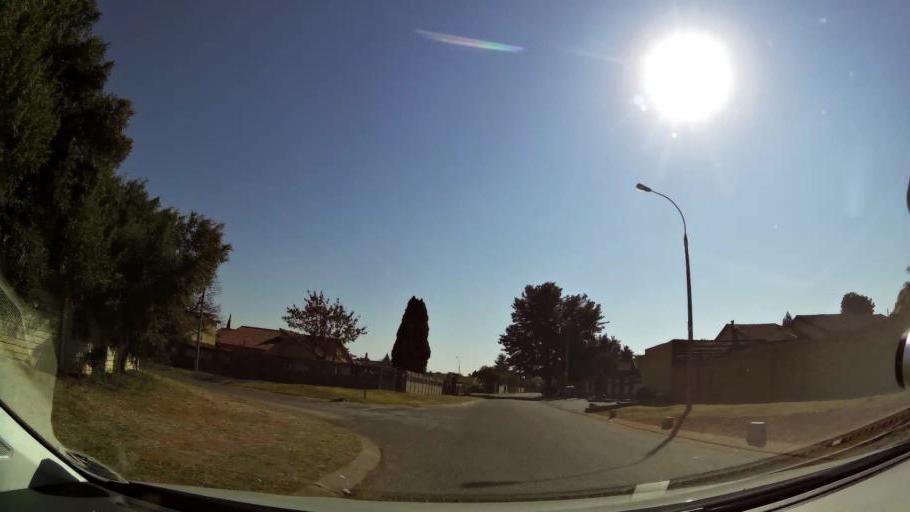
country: ZA
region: Gauteng
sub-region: City of Johannesburg Metropolitan Municipality
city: Modderfontein
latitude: -26.0504
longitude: 28.2012
